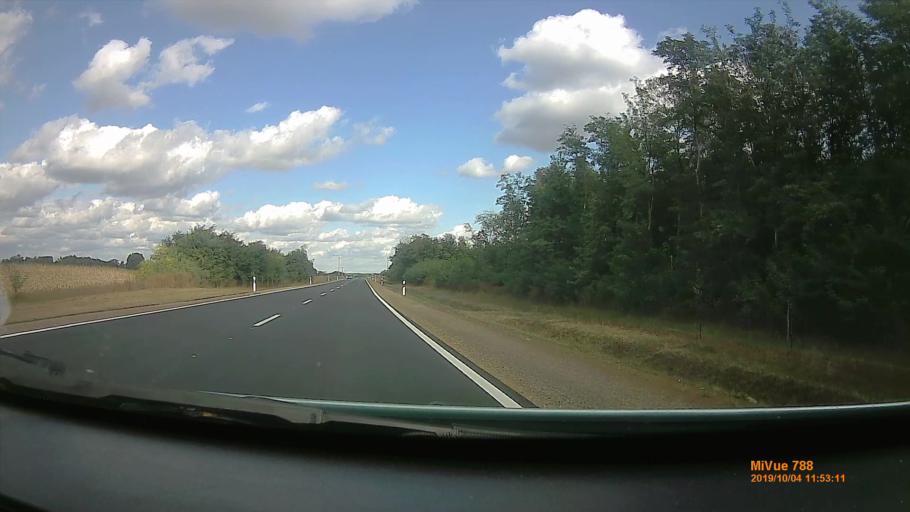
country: HU
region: Szabolcs-Szatmar-Bereg
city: Nyirtelek
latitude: 48.0066
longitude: 21.6746
